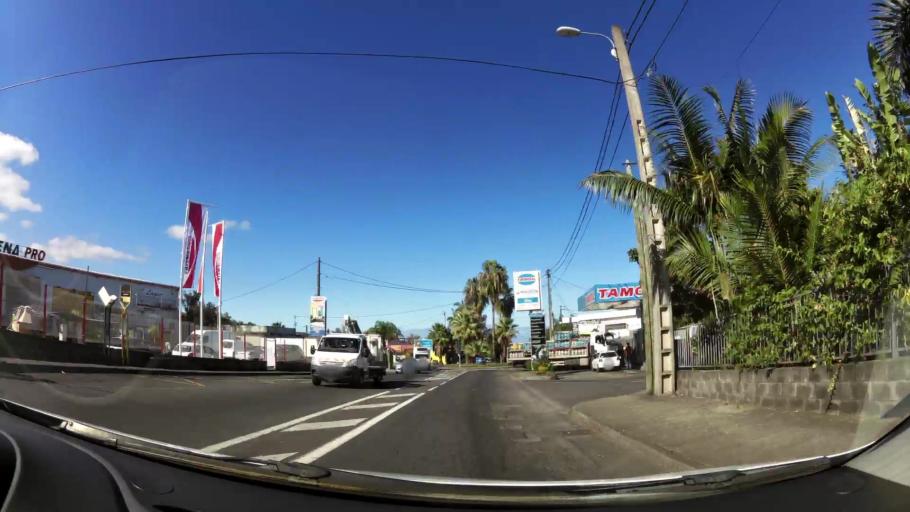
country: RE
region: Reunion
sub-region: Reunion
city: Le Tampon
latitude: -21.2784
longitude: 55.5249
